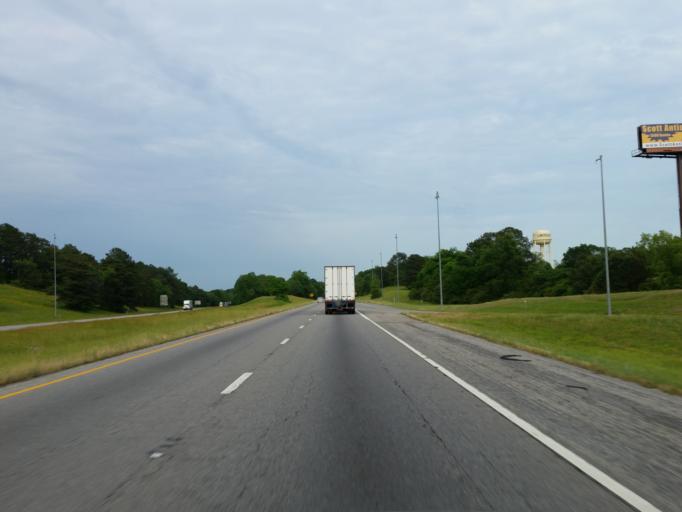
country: US
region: Alabama
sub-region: Talladega County
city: Lincoln
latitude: 33.5907
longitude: -86.1219
